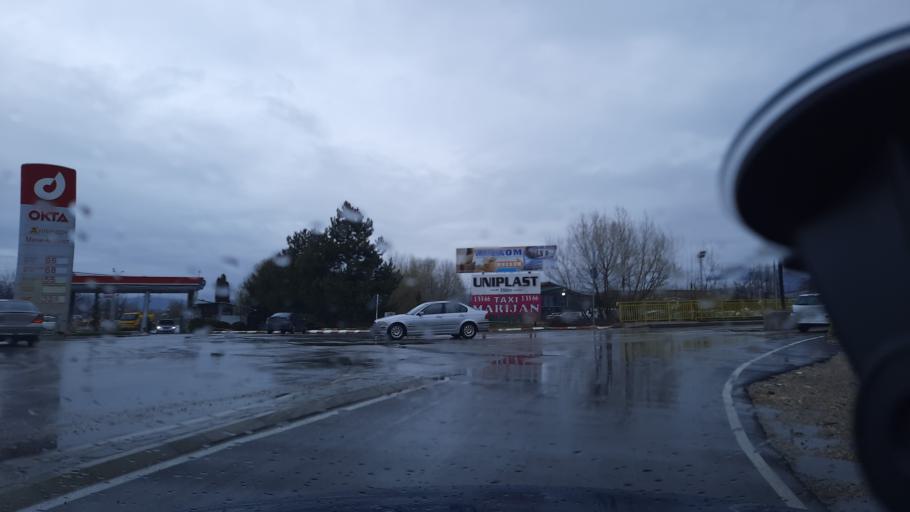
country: MK
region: Struga
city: Struga
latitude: 41.1972
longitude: 20.6762
